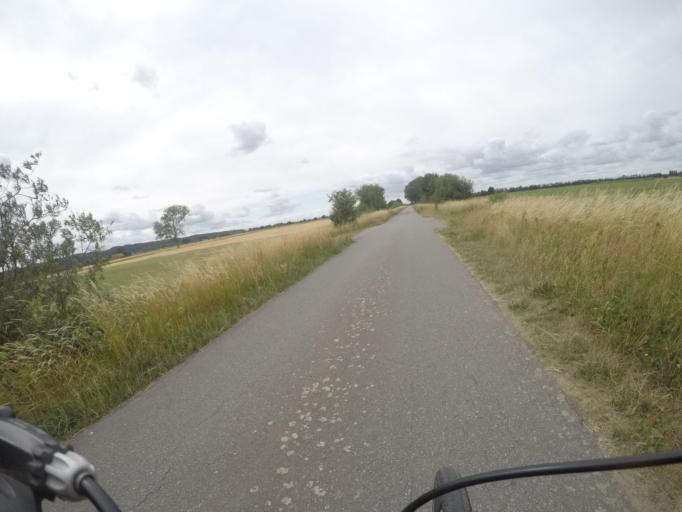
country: DE
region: Lower Saxony
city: Neu Darchau
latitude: 53.2174
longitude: 10.9628
